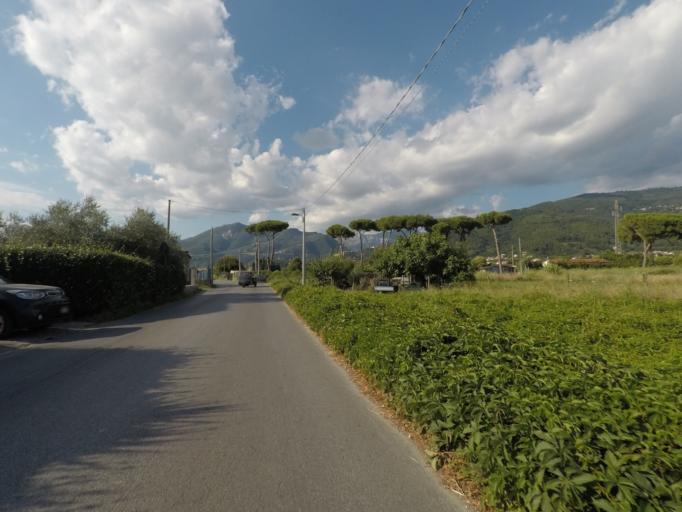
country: IT
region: Tuscany
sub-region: Provincia di Massa-Carrara
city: Massa
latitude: 44.0156
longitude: 10.1386
